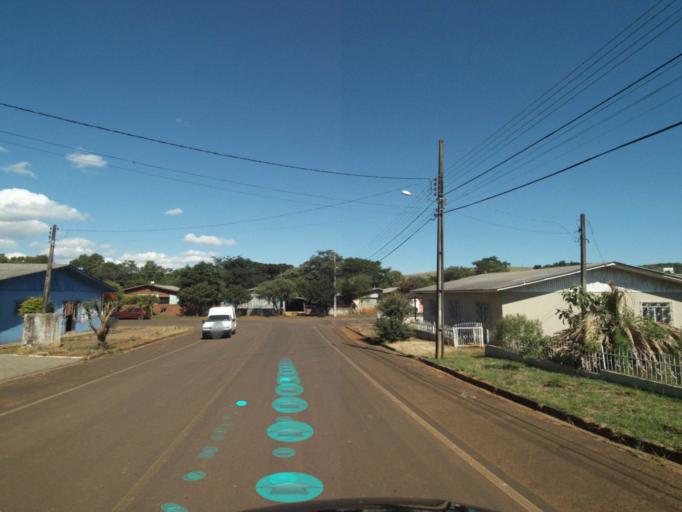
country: BR
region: Parana
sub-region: Coronel Vivida
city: Coronel Vivida
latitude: -26.1434
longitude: -52.3858
